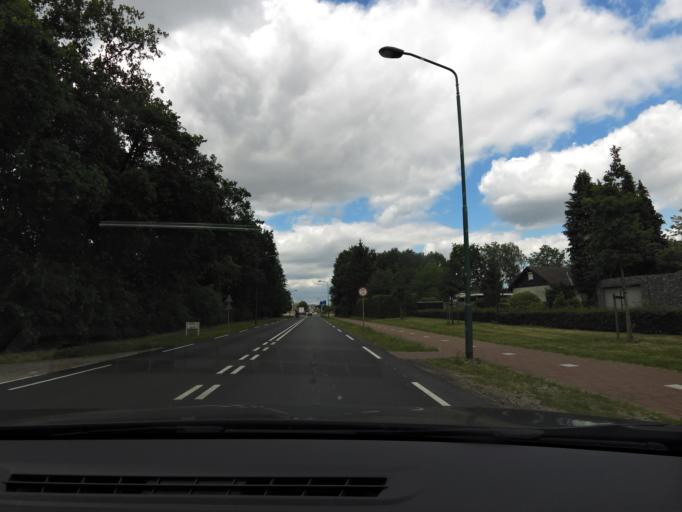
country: NL
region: North Brabant
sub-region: Gemeente Dongen
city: Dongen
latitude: 51.6269
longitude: 4.9175
